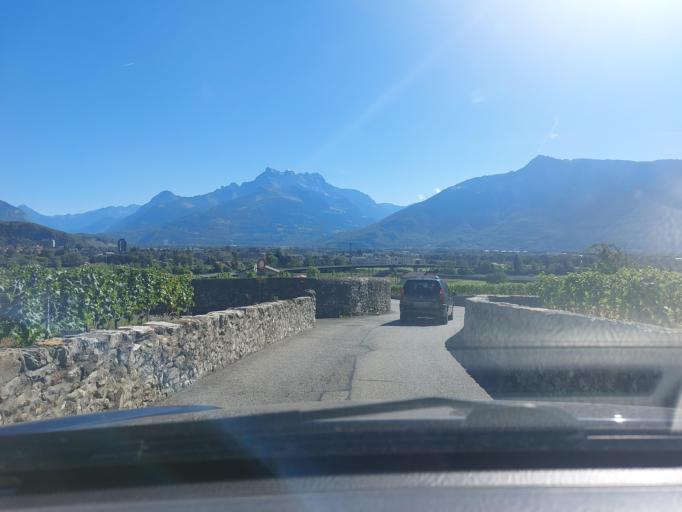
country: CH
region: Vaud
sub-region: Aigle District
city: Aigle
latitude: 46.3306
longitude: 6.9585
